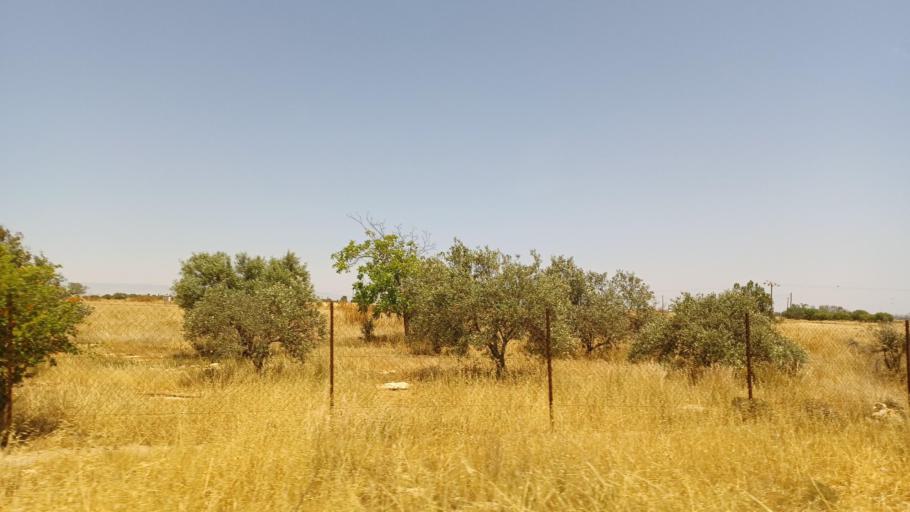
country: CY
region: Larnaka
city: Pergamos
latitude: 35.0240
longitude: 33.7108
